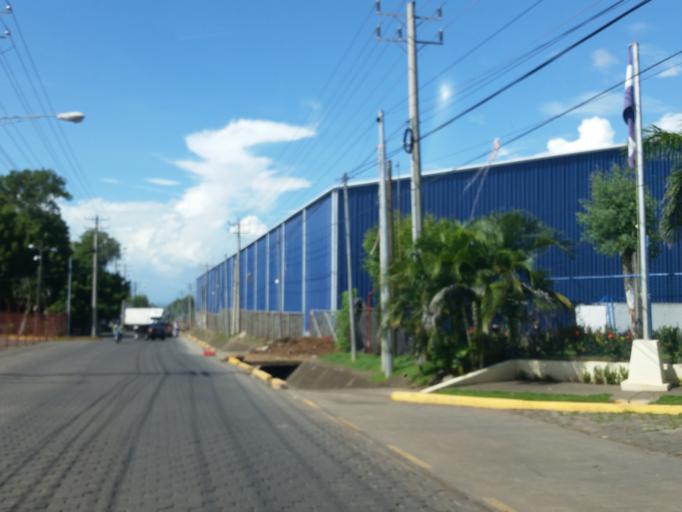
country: NI
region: Managua
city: Managua
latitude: 12.1572
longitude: -86.2237
